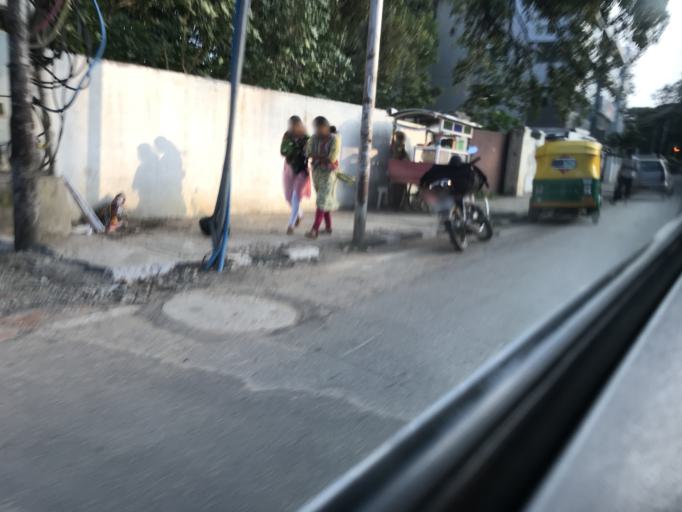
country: IN
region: Karnataka
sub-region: Bangalore Urban
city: Bangalore
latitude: 12.9917
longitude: 77.5886
